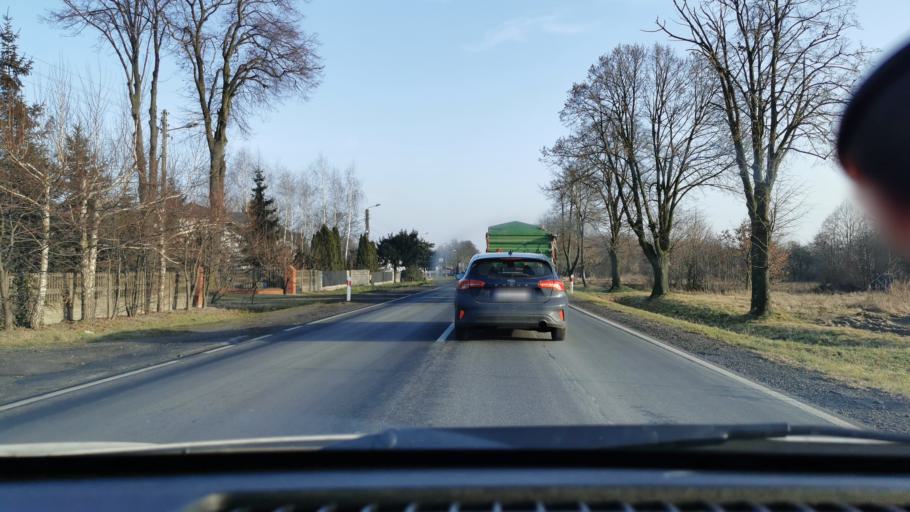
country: PL
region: Lodz Voivodeship
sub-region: Powiat sieradzki
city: Wroblew
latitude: 51.6140
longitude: 18.6081
